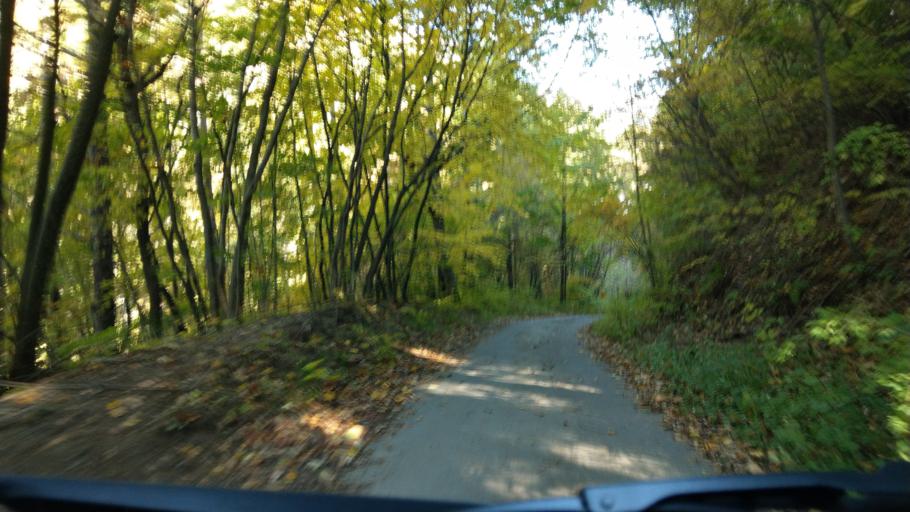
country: JP
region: Nagano
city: Komoro
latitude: 36.3774
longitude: 138.4305
